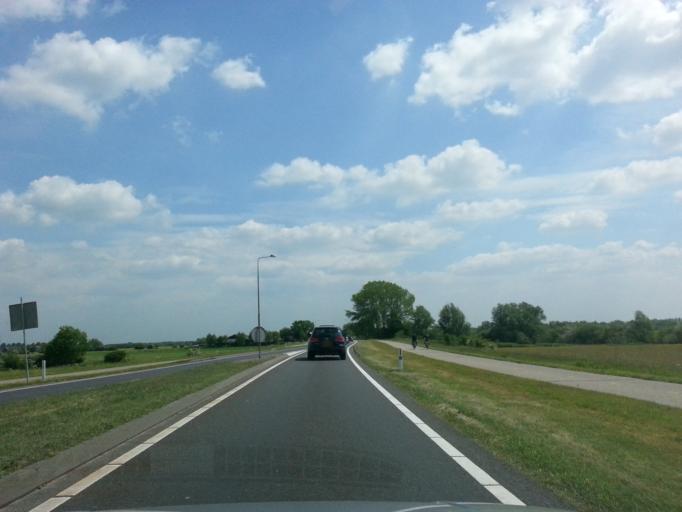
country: NL
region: Gelderland
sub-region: Gemeente Rheden
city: Ellecom
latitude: 52.0276
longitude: 6.1097
